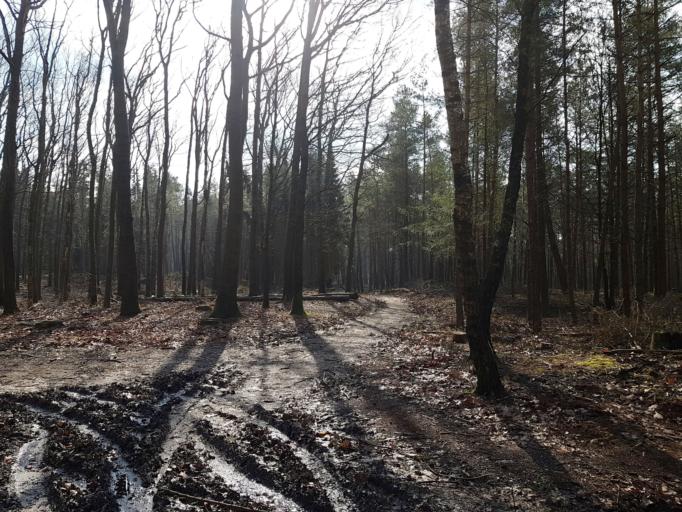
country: NL
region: Gelderland
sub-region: Gemeente Apeldoorn
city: Uddel
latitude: 52.2274
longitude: 5.8661
